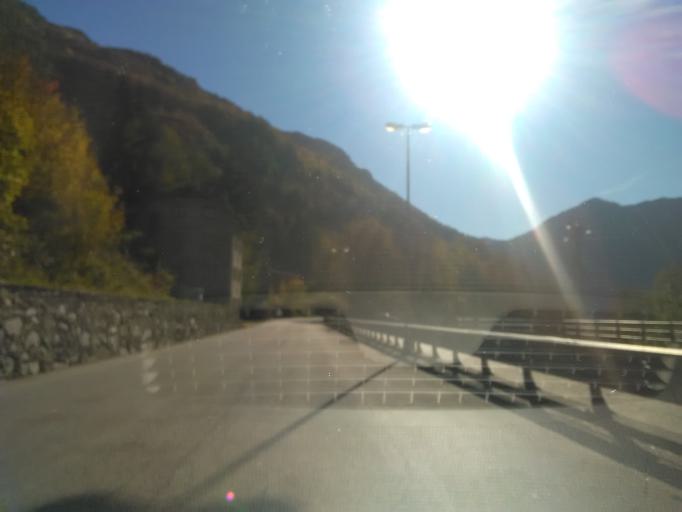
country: IT
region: Piedmont
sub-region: Provincia di Vercelli
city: Campertogno
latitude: 45.7937
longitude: 8.0355
